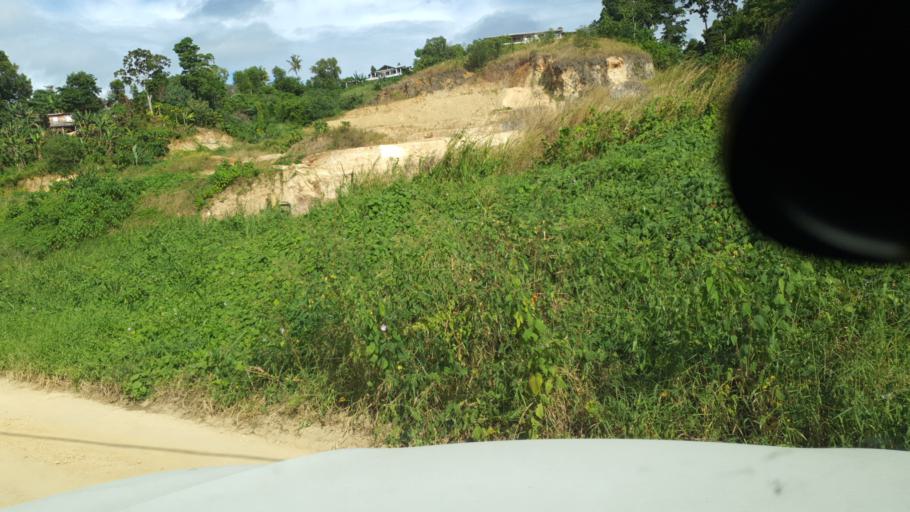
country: SB
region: Guadalcanal
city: Honiara
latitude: -9.4369
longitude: 159.9282
